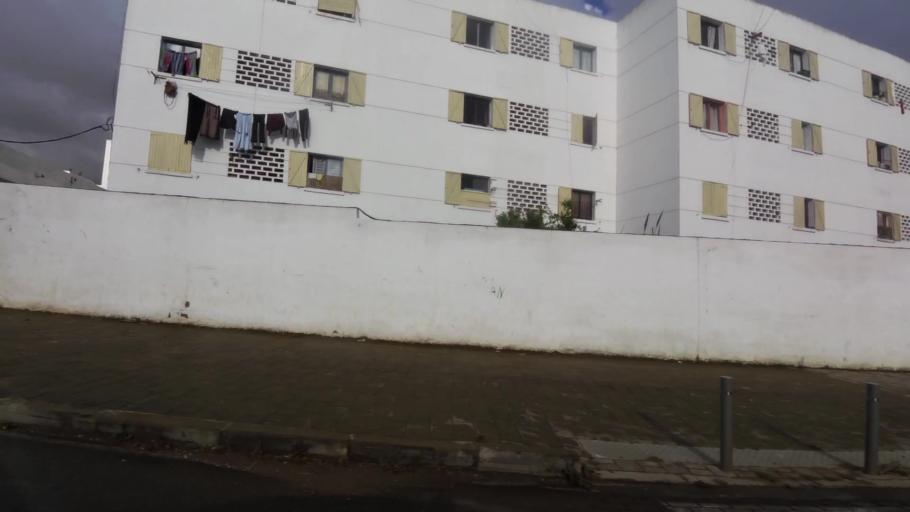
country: MA
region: Grand Casablanca
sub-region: Casablanca
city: Casablanca
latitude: 33.5517
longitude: -7.6517
